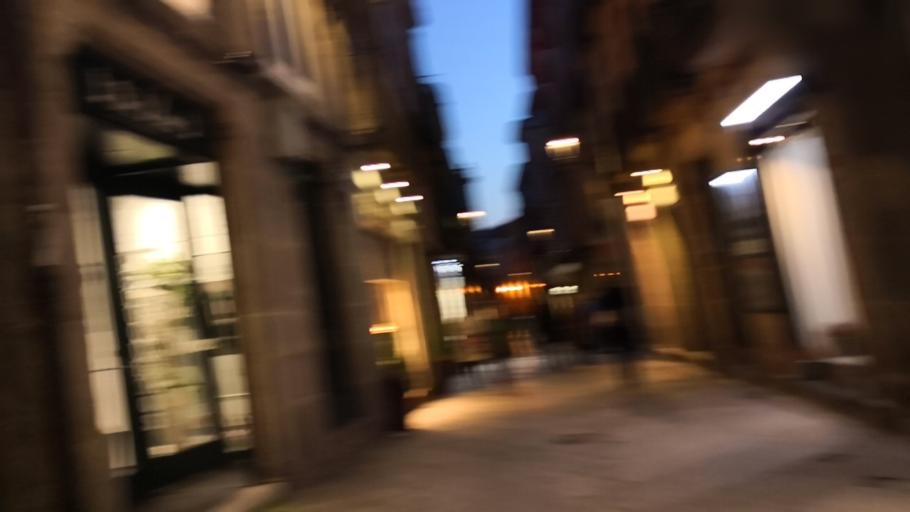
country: ES
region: Galicia
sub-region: Provincia de Ourense
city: Ourense
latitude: 42.3373
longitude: -7.8635
